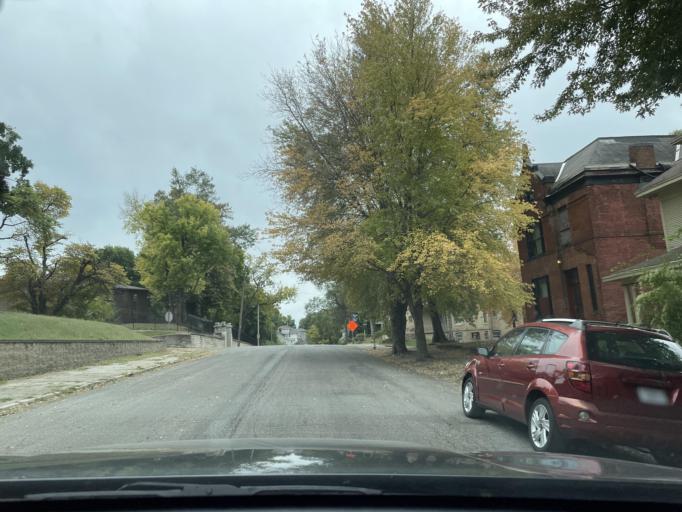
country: US
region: Missouri
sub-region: Buchanan County
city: Saint Joseph
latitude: 39.7639
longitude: -94.8454
